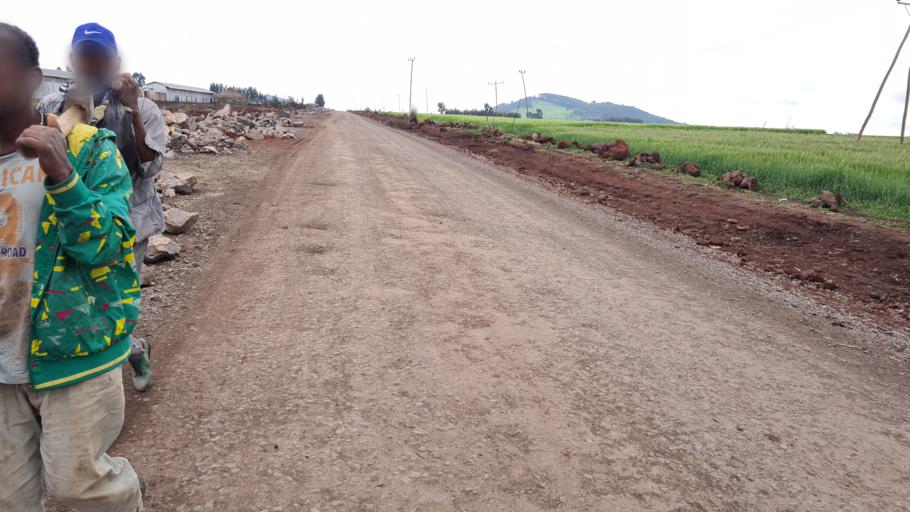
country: ET
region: Oromiya
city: Huruta
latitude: 8.0801
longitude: 39.5448
